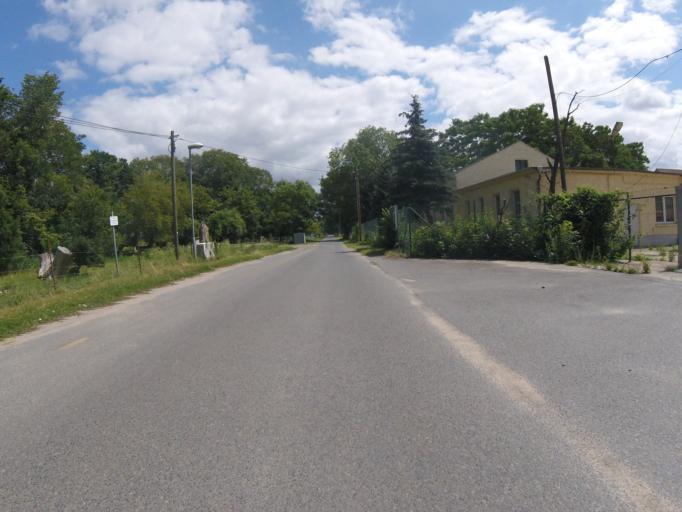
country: DE
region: Brandenburg
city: Mittenwalde
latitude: 52.2417
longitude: 13.5300
